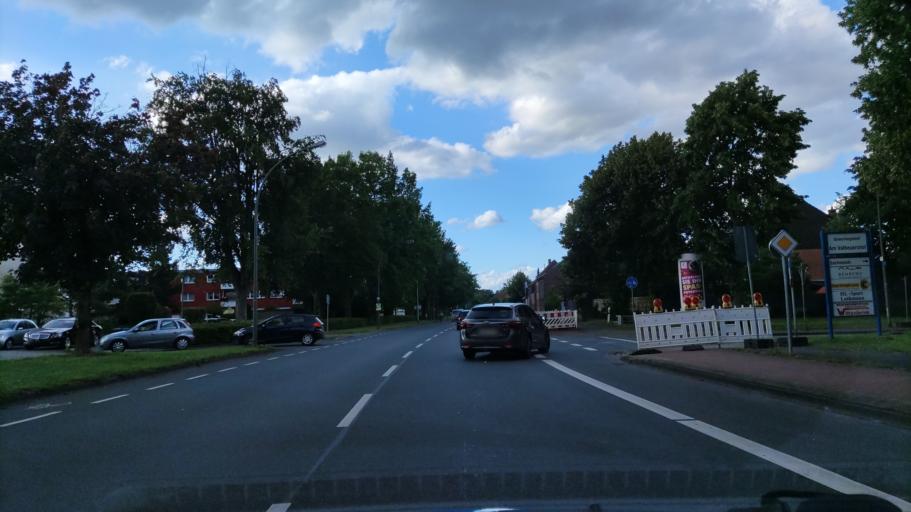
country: DE
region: North Rhine-Westphalia
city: Ahlen
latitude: 51.7500
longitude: 7.8978
